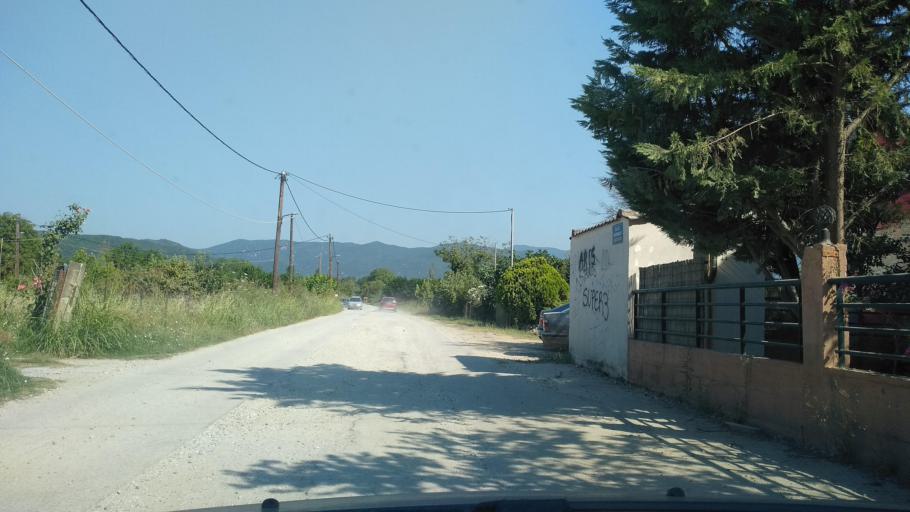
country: GR
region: Central Macedonia
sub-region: Nomos Thessalonikis
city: Stavros
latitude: 40.6725
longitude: 23.6911
